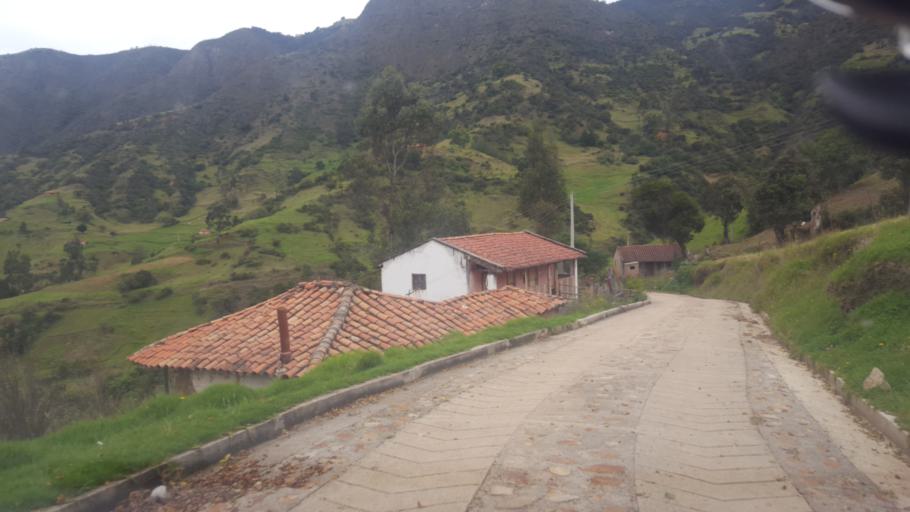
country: CO
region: Boyaca
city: Belen
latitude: 6.0213
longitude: -72.8778
